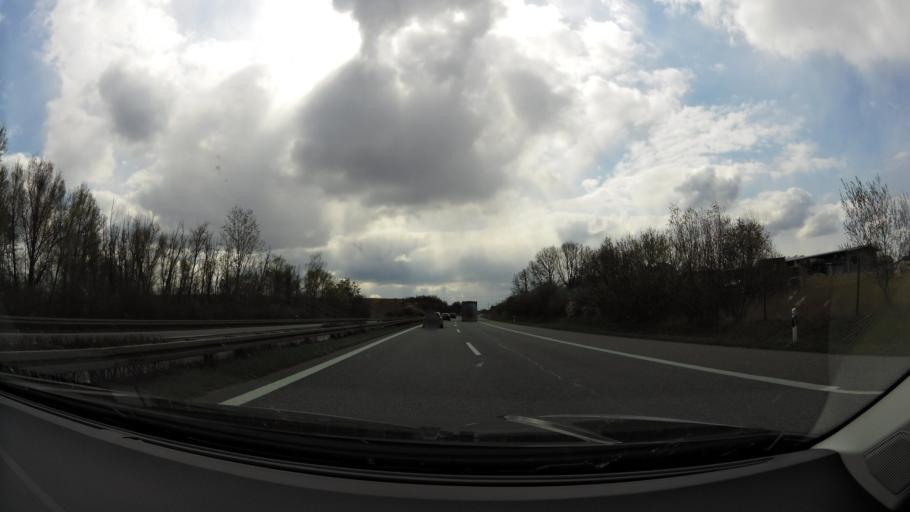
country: DE
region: Mecklenburg-Vorpommern
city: Lalendorf
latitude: 53.6824
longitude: 12.3697
